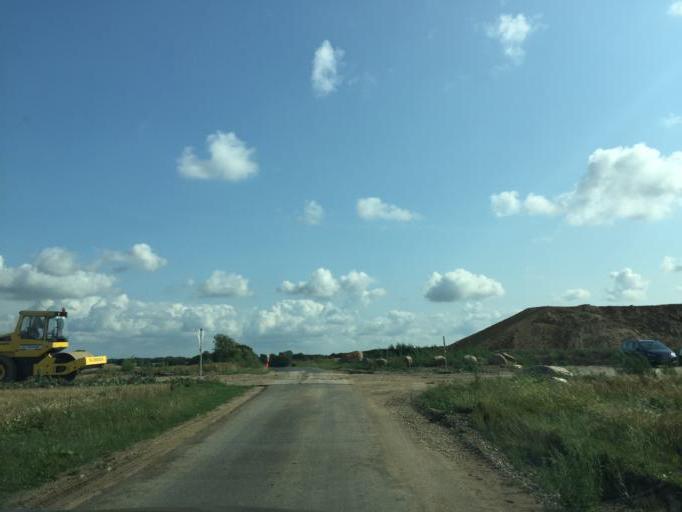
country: DK
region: South Denmark
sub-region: Odense Kommune
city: Bellinge
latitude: 55.3261
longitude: 10.3708
